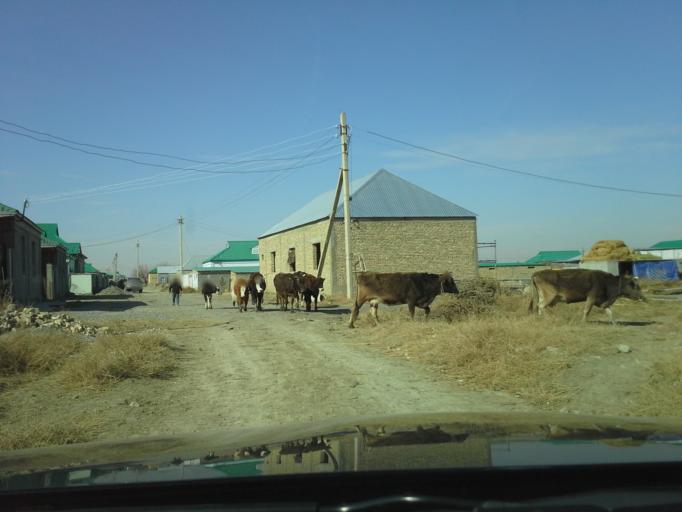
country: TM
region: Ahal
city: Abadan
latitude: 38.1025
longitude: 58.0332
